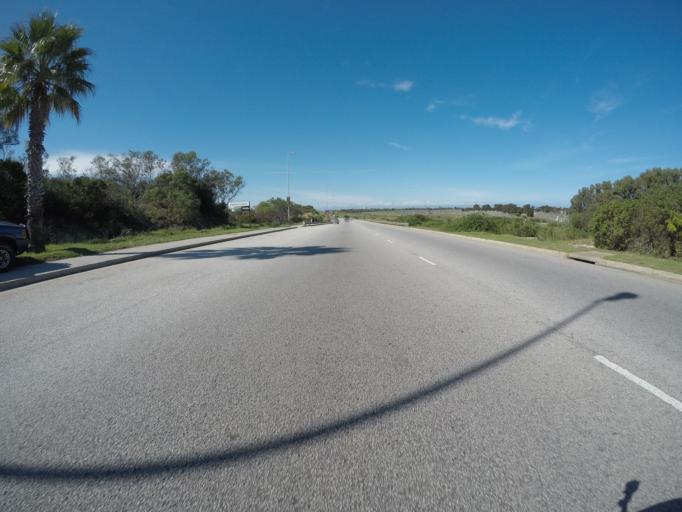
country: ZA
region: Eastern Cape
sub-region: Nelson Mandela Bay Metropolitan Municipality
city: Port Elizabeth
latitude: -33.9841
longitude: 25.6387
